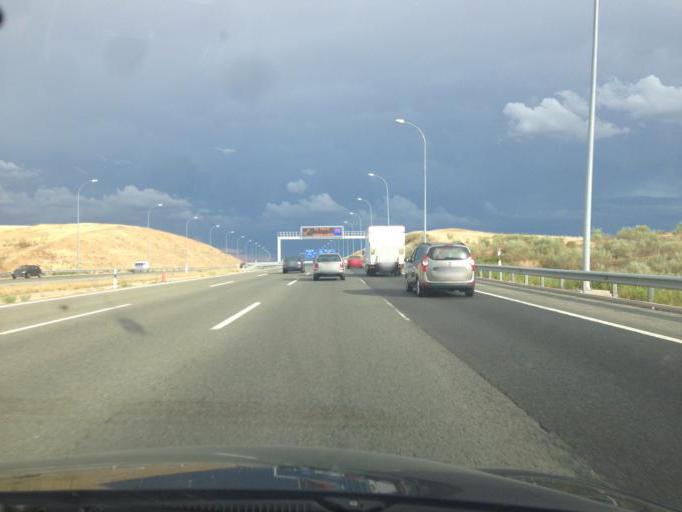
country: ES
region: Madrid
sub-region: Provincia de Madrid
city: Paracuellos de Jarama
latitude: 40.5294
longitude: -3.5179
